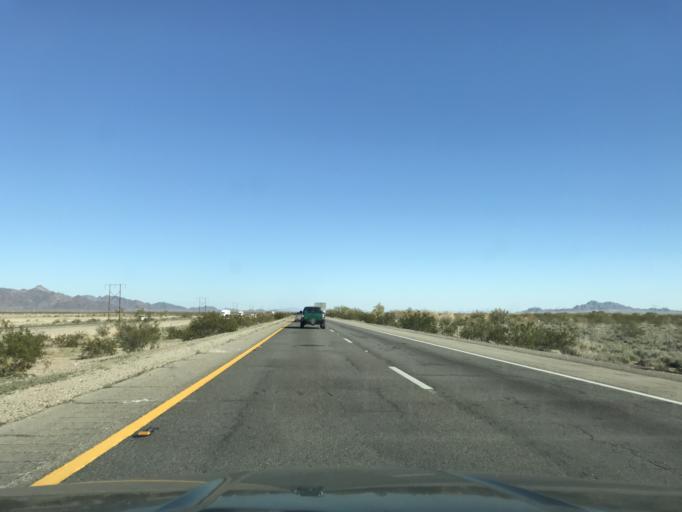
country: US
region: California
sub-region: Riverside County
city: Mesa Verde
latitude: 33.6058
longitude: -114.9694
